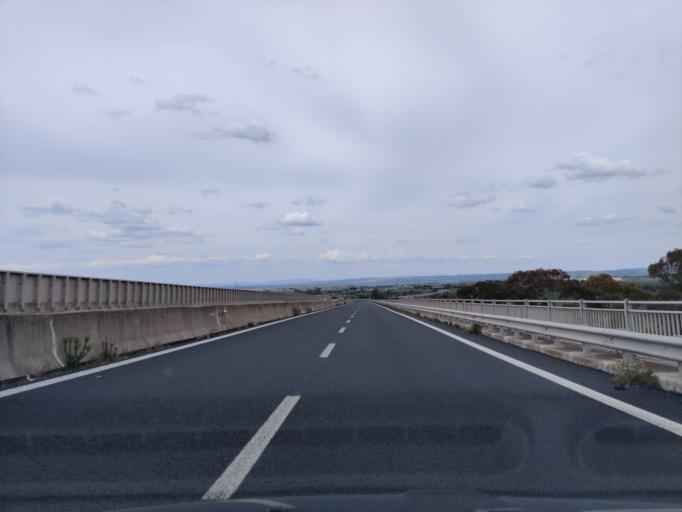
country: IT
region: Latium
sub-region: Citta metropolitana di Roma Capitale
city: Aurelia
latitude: 42.1412
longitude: 11.7936
